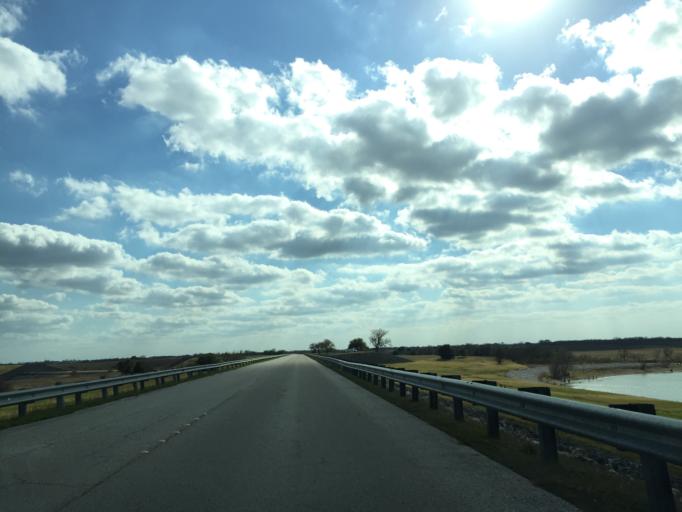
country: US
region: Texas
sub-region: Williamson County
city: Granger
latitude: 30.6884
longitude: -97.3363
